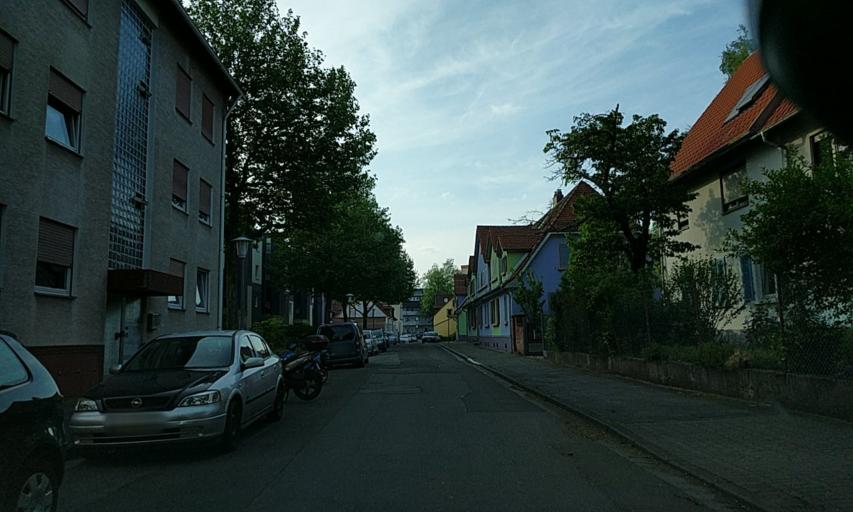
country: DE
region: Rheinland-Pfalz
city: Kaiserslautern
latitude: 49.4475
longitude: 7.7870
